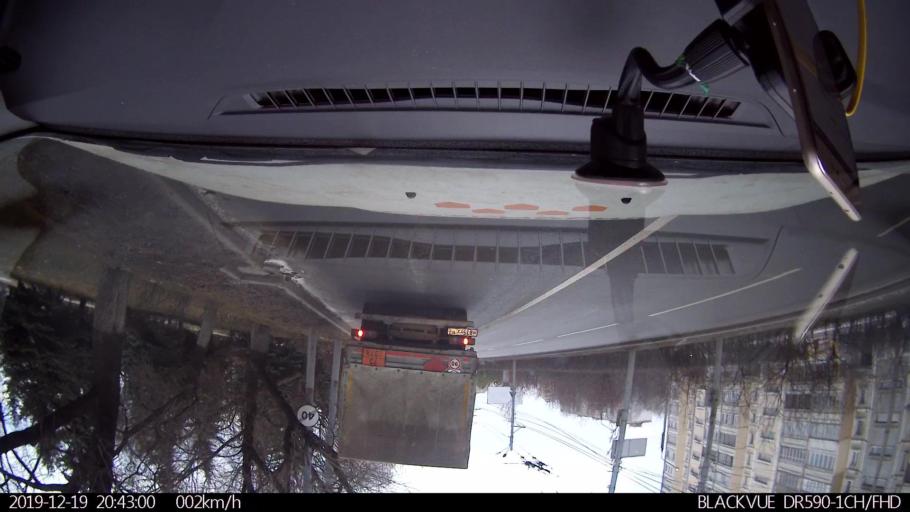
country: RU
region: Nizjnij Novgorod
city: Nizhniy Novgorod
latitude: 56.3243
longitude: 43.8805
